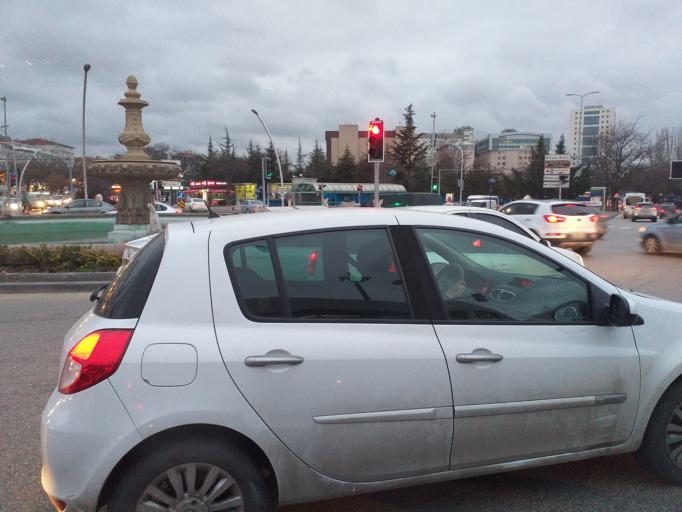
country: TR
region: Ankara
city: Ankara
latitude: 39.9329
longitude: 32.8294
